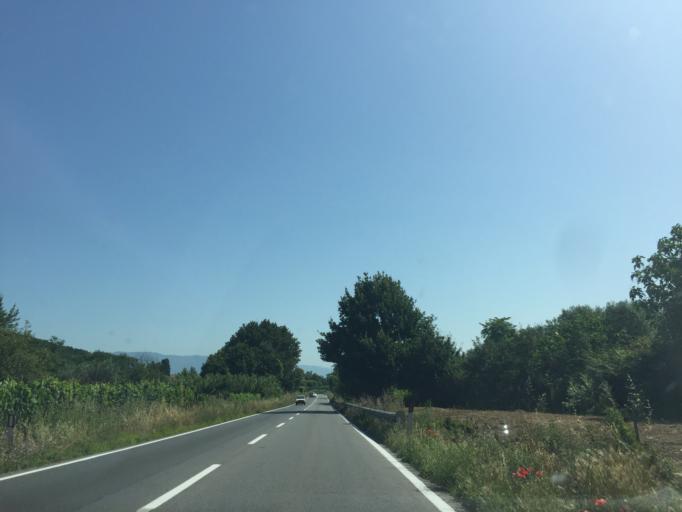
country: IT
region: Tuscany
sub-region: Province of Pisa
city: Asciano
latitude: 43.7883
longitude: 10.4722
